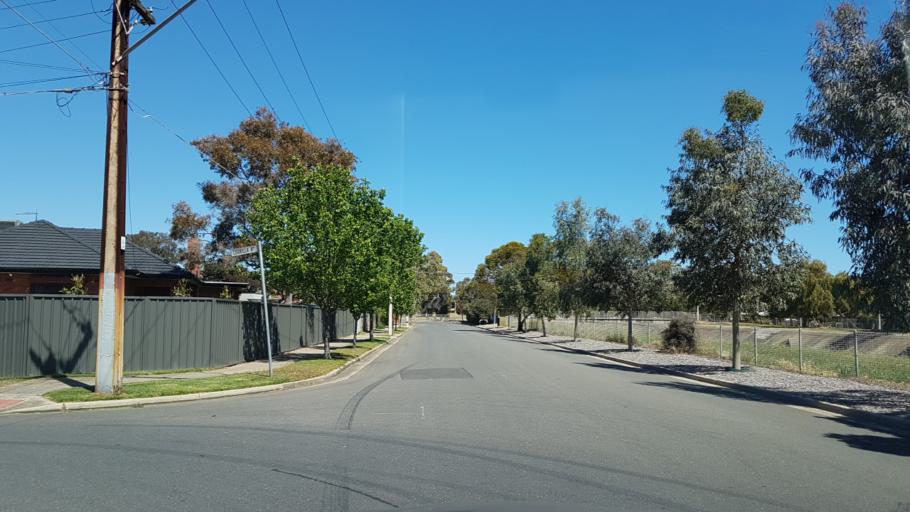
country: AU
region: South Australia
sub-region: Holdfast Bay
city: Glenelg East
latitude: -34.9698
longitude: 138.5247
